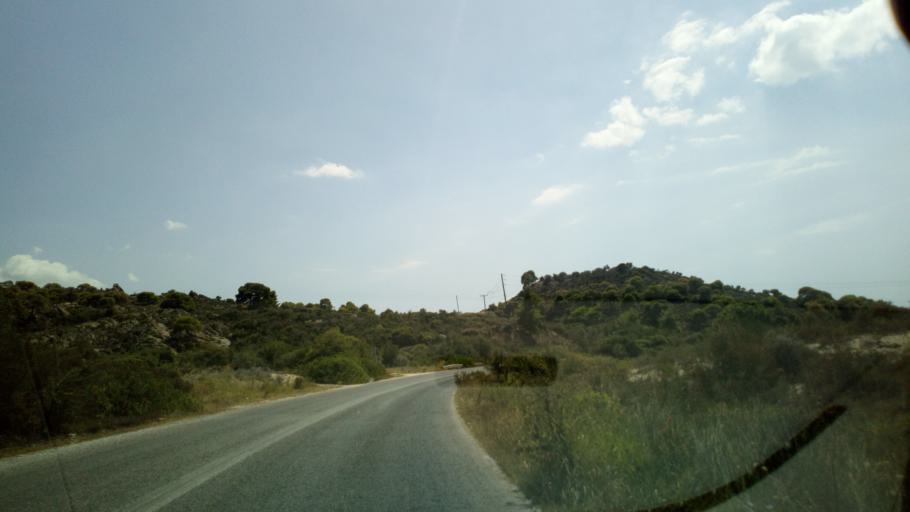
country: GR
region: Central Macedonia
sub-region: Nomos Chalkidikis
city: Agios Nikolaos
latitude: 40.2224
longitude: 23.7019
